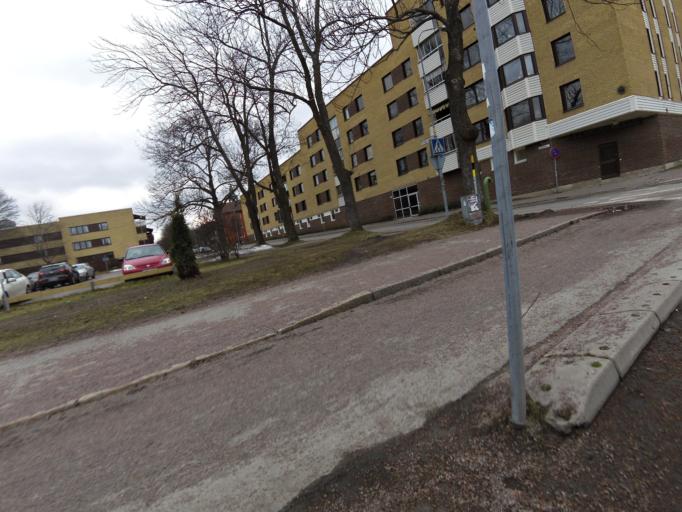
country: SE
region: Gaevleborg
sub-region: Gavle Kommun
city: Gavle
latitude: 60.6736
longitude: 17.1652
